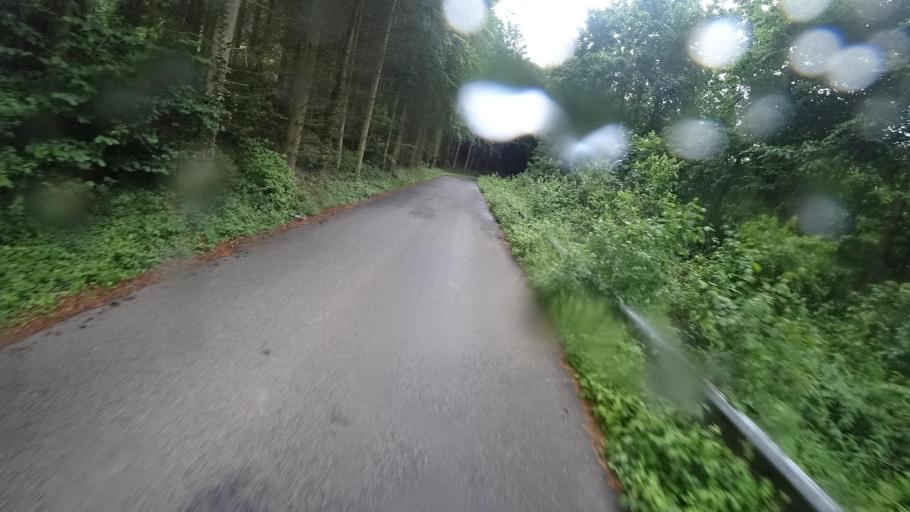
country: DE
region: Rheinland-Pfalz
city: Dernau
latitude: 50.5433
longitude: 7.0645
